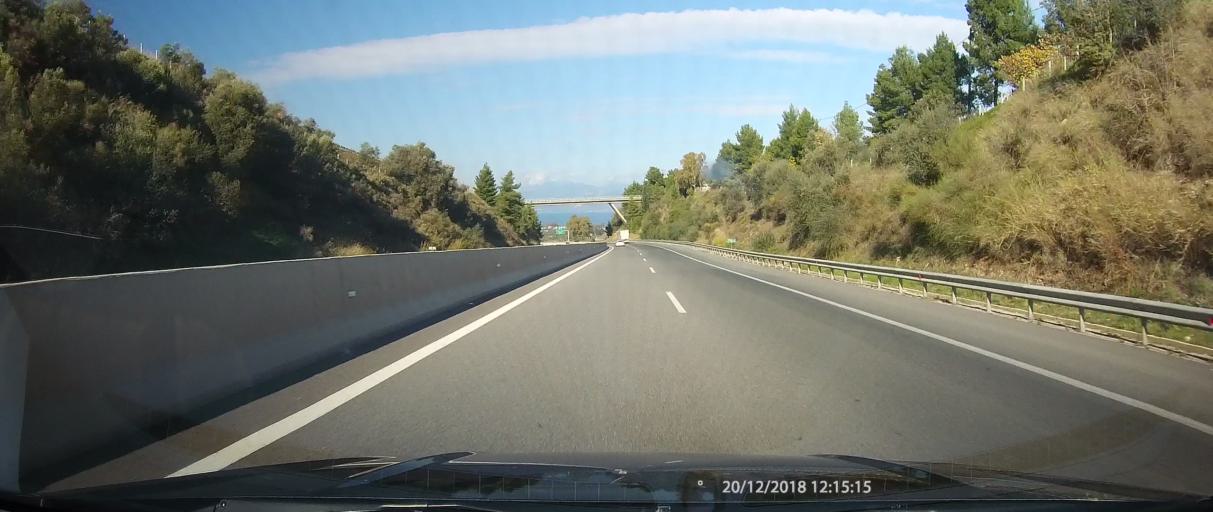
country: GR
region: West Greece
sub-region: Nomos Achaias
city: Aigio
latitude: 38.2503
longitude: 22.0707
